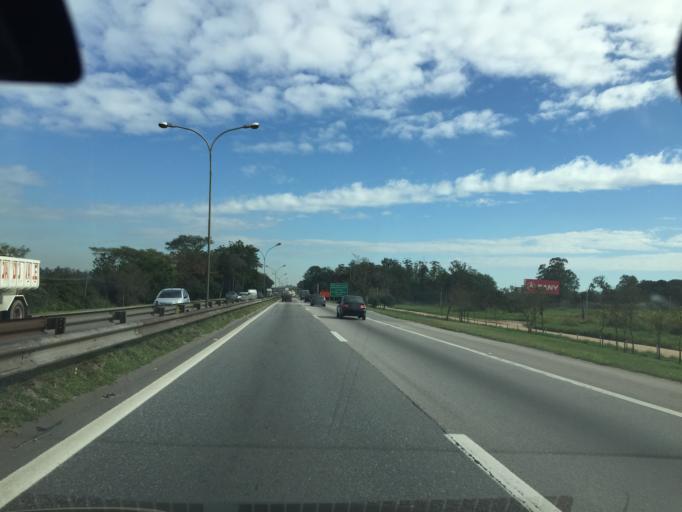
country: BR
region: Sao Paulo
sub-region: Jacarei
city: Jacarei
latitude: -23.2709
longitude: -45.9679
